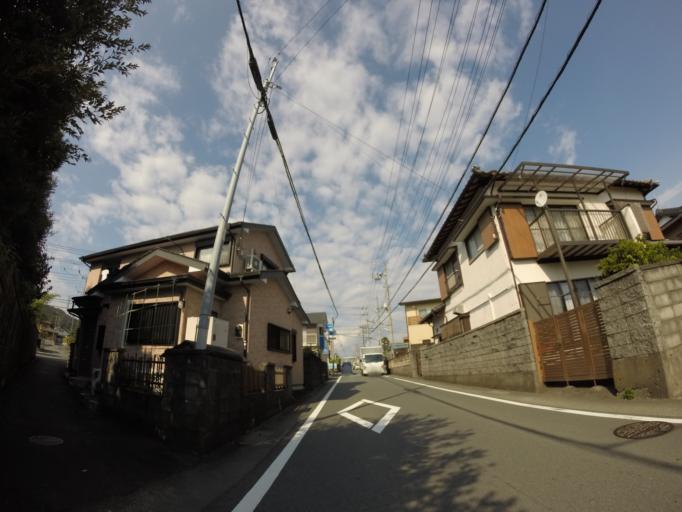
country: JP
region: Shizuoka
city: Fujinomiya
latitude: 35.1911
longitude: 138.6441
